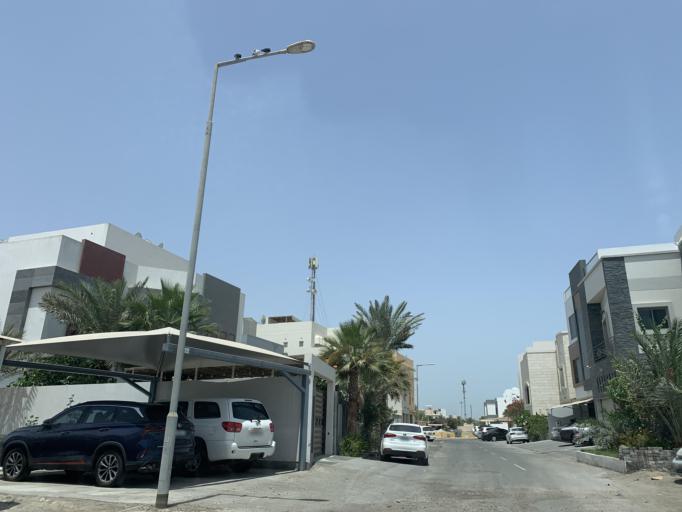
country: BH
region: Northern
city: Sitrah
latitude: 26.1424
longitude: 50.5912
